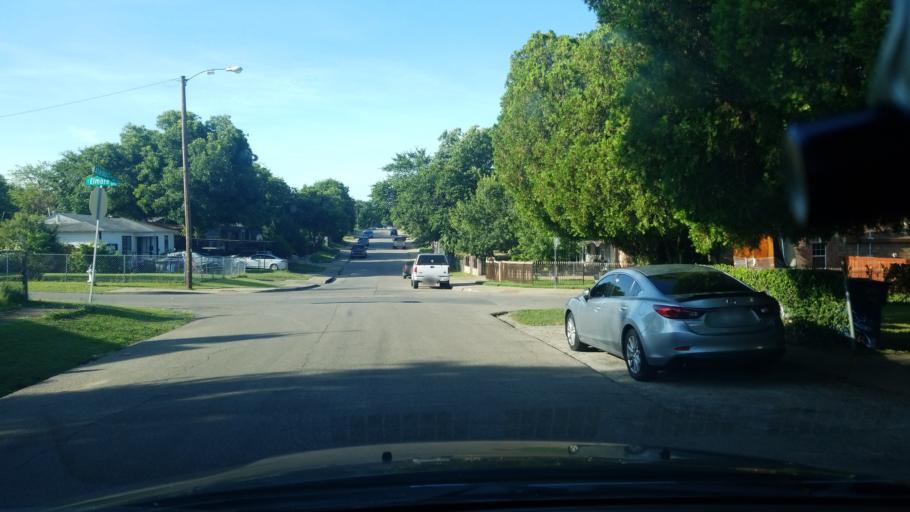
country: US
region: Texas
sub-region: Dallas County
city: Dallas
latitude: 32.7170
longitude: -96.8158
